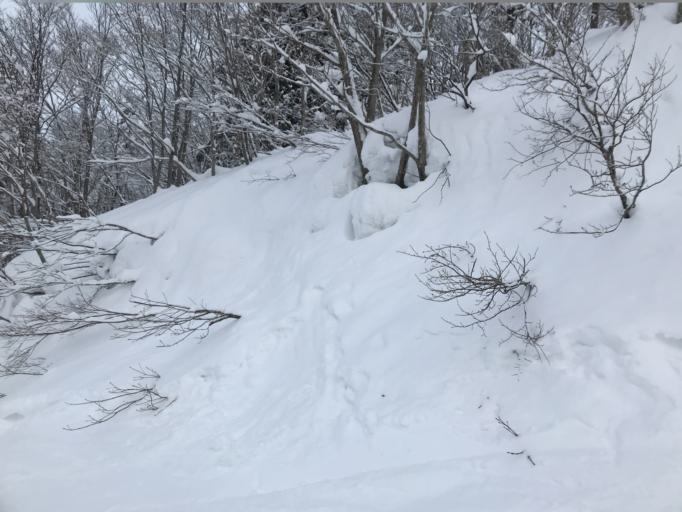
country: JP
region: Nagano
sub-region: Kitaazumi Gun
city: Hakuba
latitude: 36.7013
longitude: 137.8179
